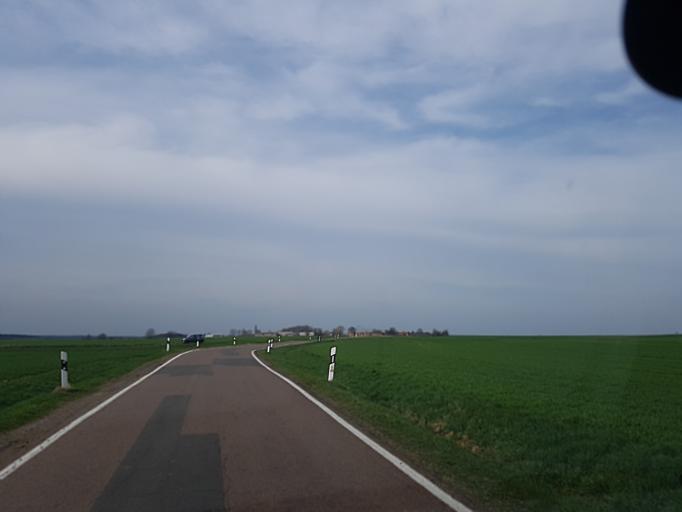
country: DE
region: Saxony
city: Strehla
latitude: 51.3569
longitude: 13.1895
